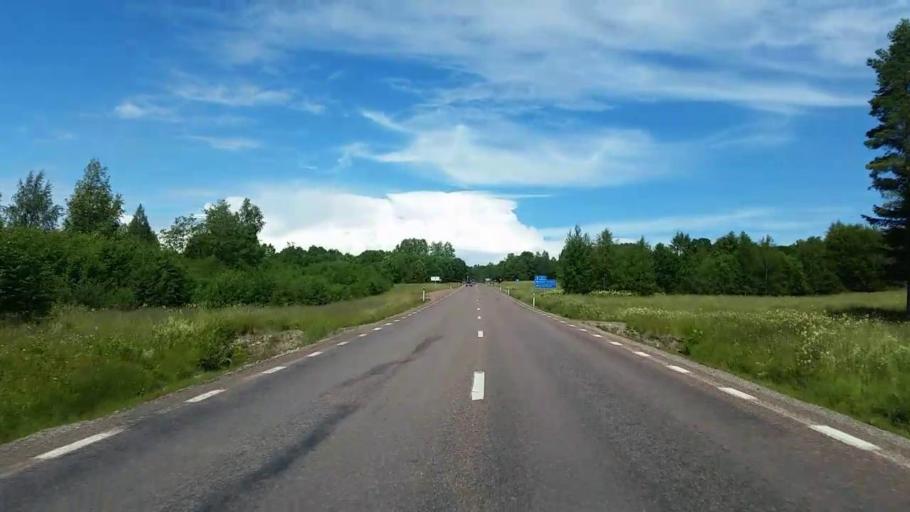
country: SE
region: Dalarna
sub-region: Rattviks Kommun
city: Raettvik
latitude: 60.9996
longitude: 15.2187
